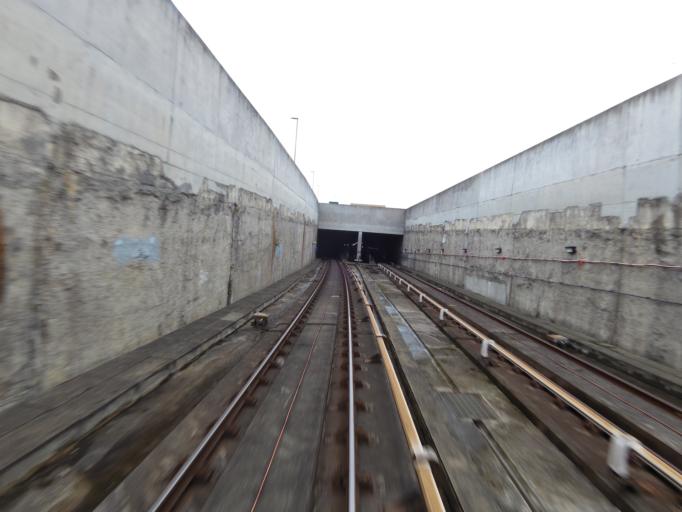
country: GB
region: England
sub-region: Greater London
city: Woolwich
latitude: 51.5019
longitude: 0.0650
